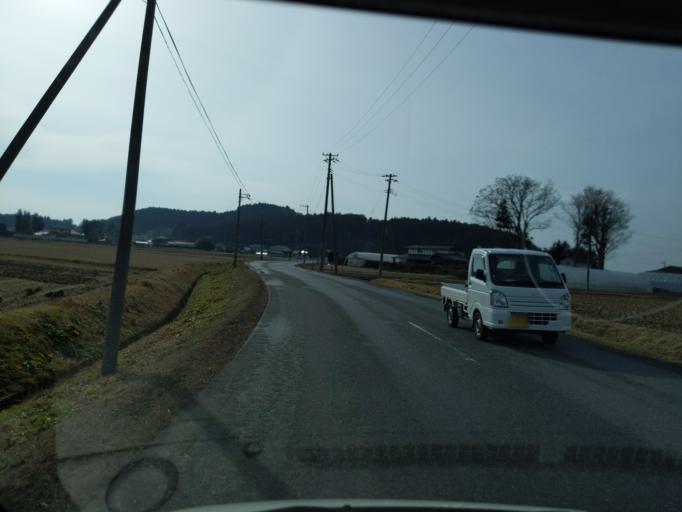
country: JP
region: Iwate
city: Ichinoseki
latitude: 38.7793
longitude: 141.1762
